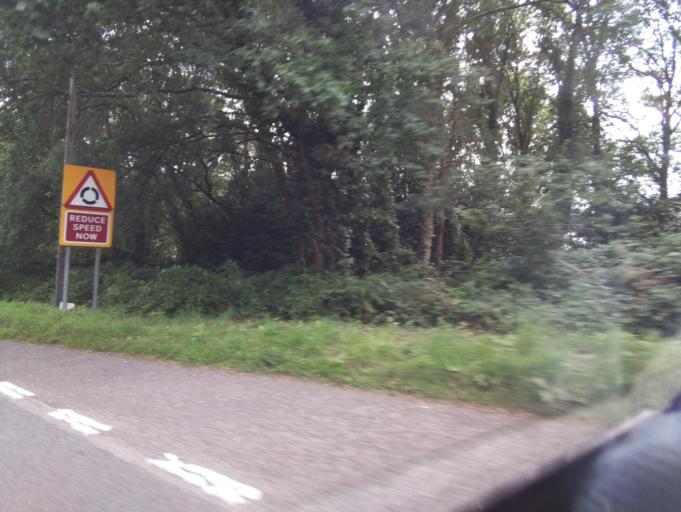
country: GB
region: England
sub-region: Hampshire
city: Marchwood
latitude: 50.8668
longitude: -1.4380
